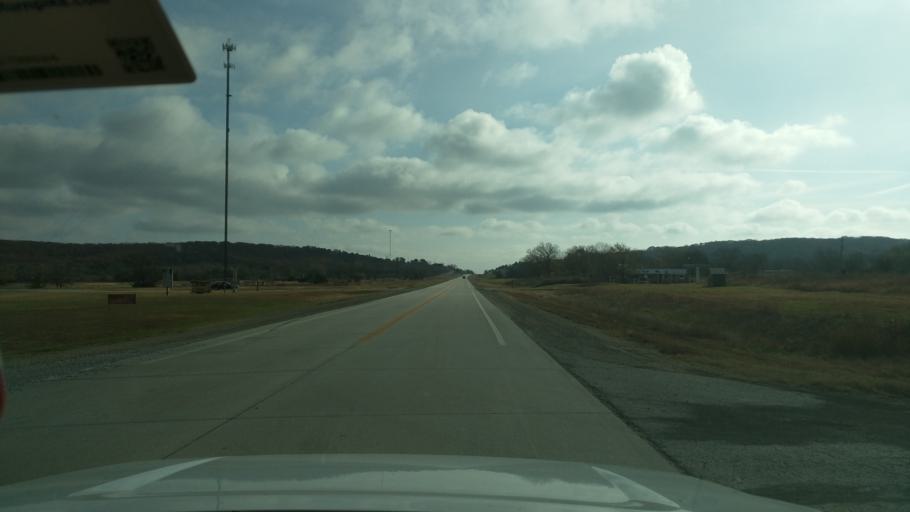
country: US
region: Kansas
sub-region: Chautauqua County
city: Sedan
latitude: 37.0786
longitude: -96.0962
